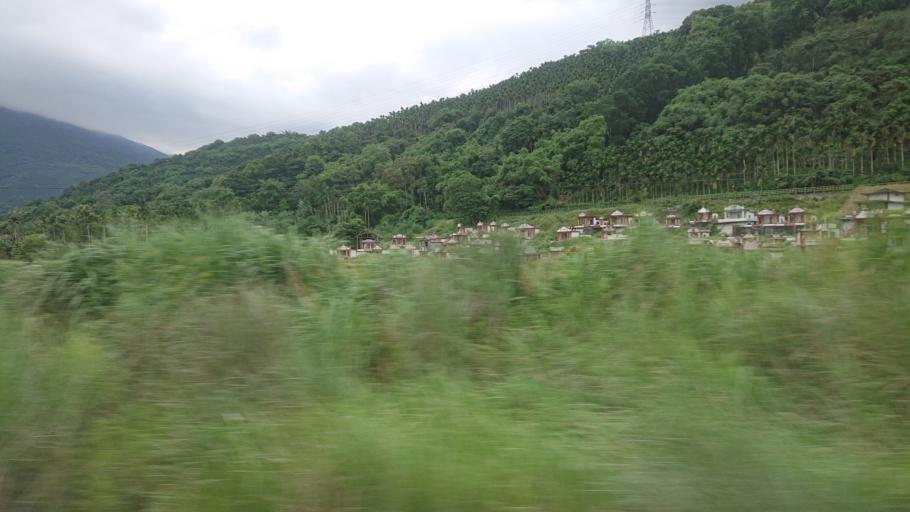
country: TW
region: Taiwan
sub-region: Hualien
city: Hualian
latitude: 23.5849
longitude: 121.3813
